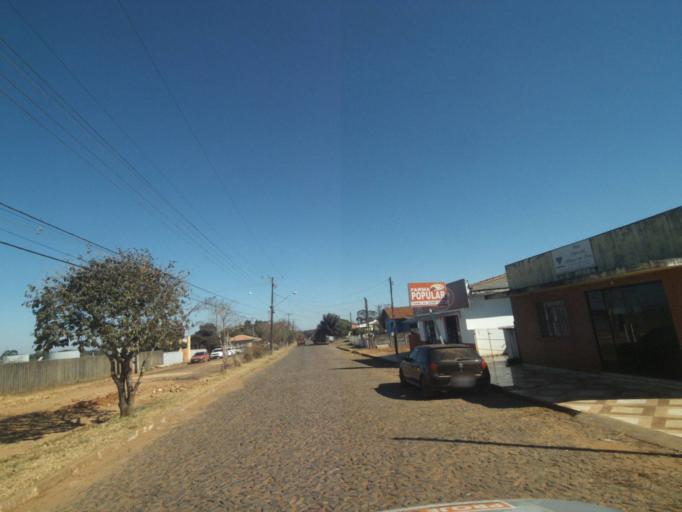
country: BR
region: Parana
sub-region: Reserva
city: Reserva
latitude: -24.6229
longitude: -50.6400
